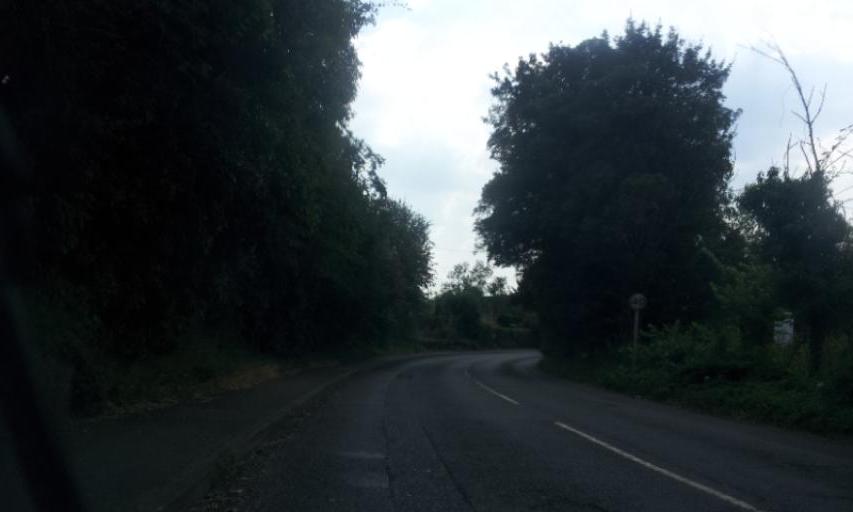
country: GB
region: England
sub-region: Kent
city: Yalding
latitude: 51.2174
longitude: 0.4208
